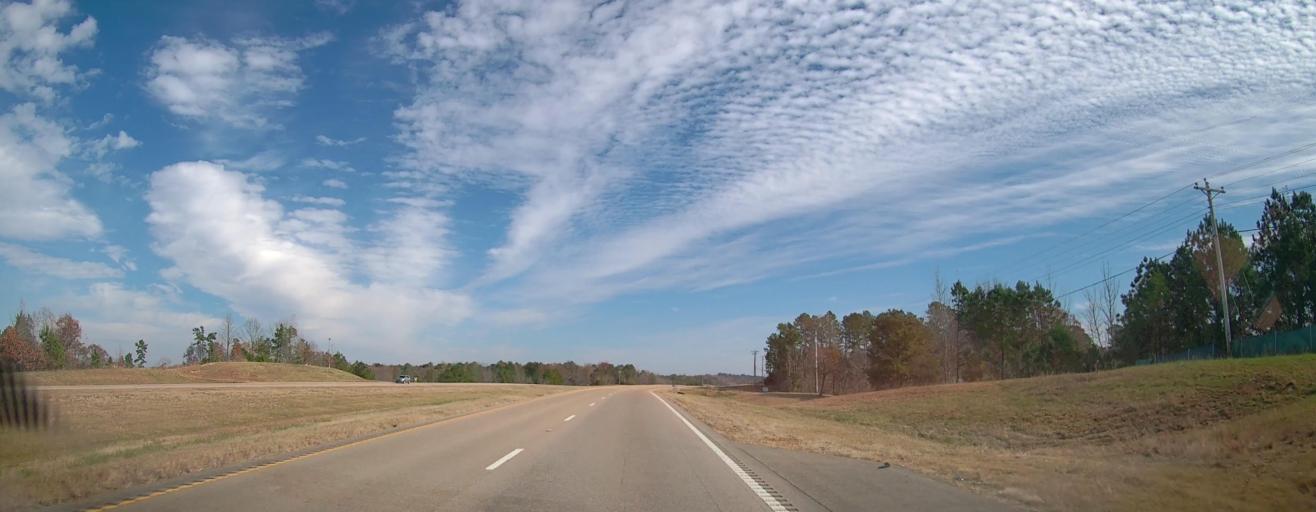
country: US
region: Mississippi
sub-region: Benton County
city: Ashland
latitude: 34.9548
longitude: -88.9914
